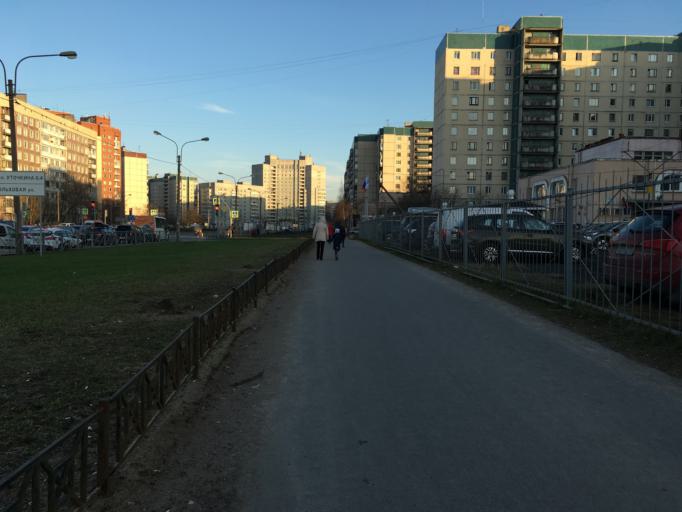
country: RU
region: St.-Petersburg
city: Komendantsky aerodrom
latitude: 60.0157
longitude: 30.2598
